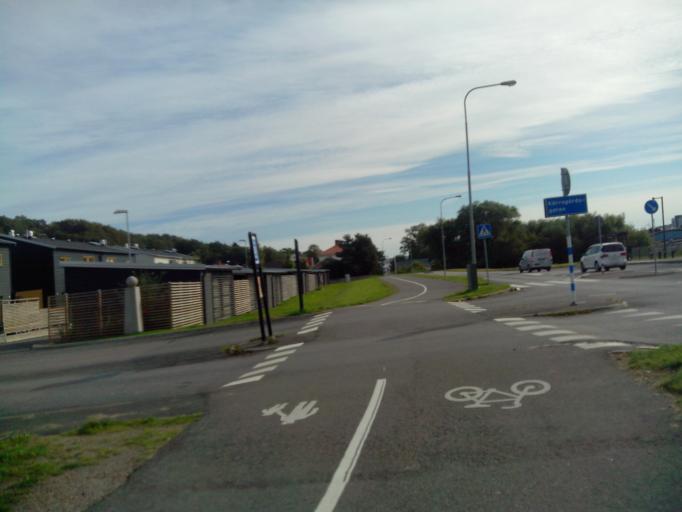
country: SE
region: Vaestra Goetaland
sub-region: Goteborg
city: Goeteborg
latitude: 57.7347
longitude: 11.9577
